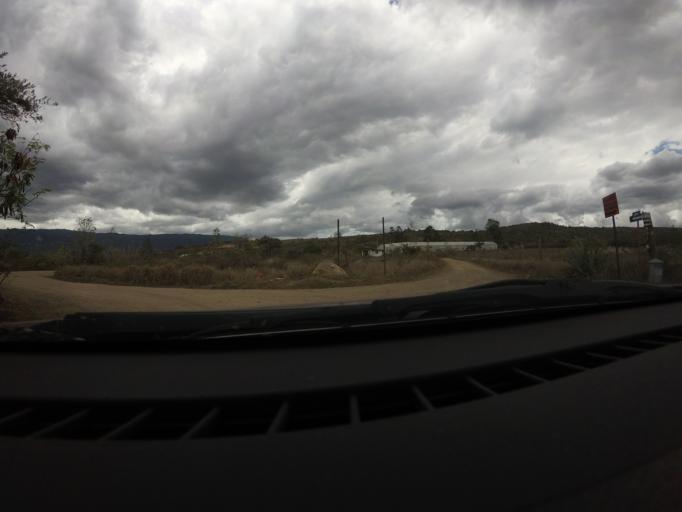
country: CO
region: Boyaca
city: Villa de Leiva
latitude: 5.6465
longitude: -73.5595
